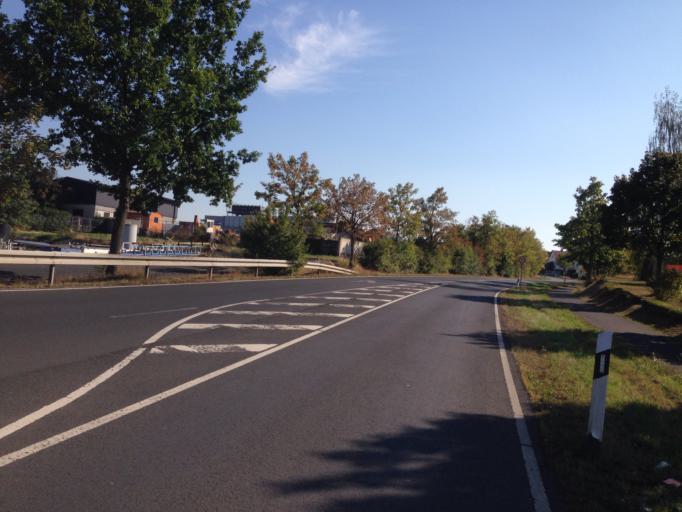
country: DE
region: Hesse
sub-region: Regierungsbezirk Giessen
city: Giessen
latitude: 50.5420
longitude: 8.7068
